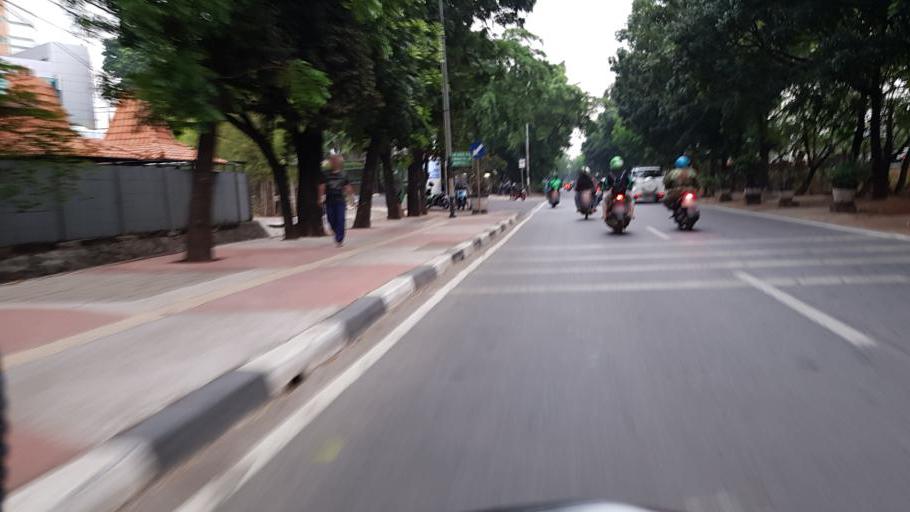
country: ID
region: Jakarta Raya
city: Jakarta
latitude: -6.3072
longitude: 106.8938
